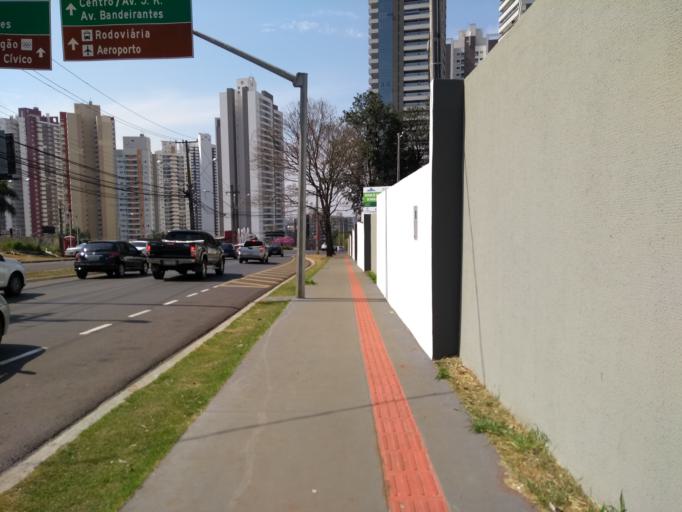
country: BR
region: Parana
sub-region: Londrina
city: Londrina
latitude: -23.3357
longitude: -51.1786
